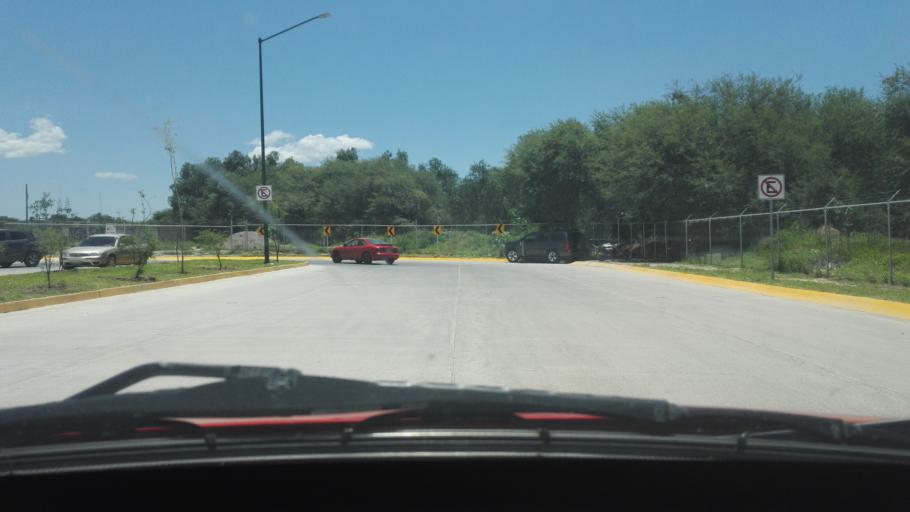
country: MX
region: Guanajuato
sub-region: Leon
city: Ladrilleras del Refugio
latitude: 21.0582
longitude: -101.5656
